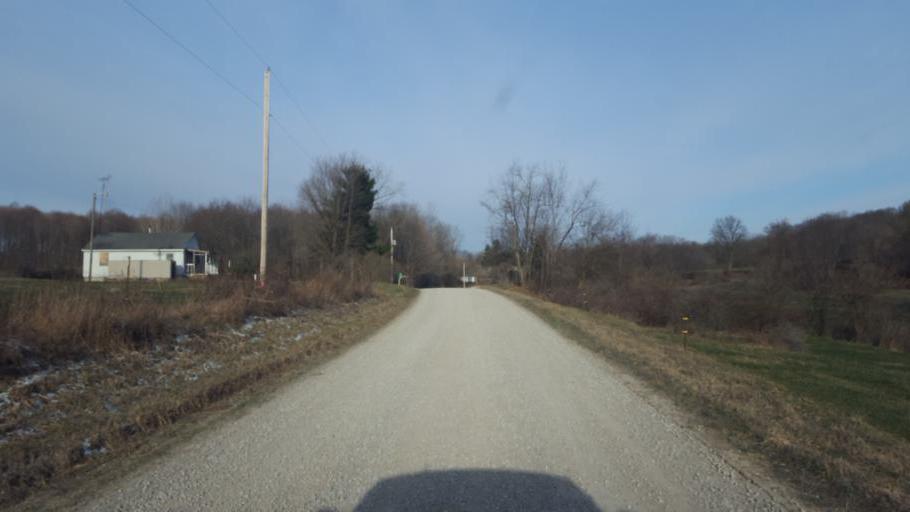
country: US
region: Ohio
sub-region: Richland County
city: Lexington
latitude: 40.5690
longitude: -82.6565
